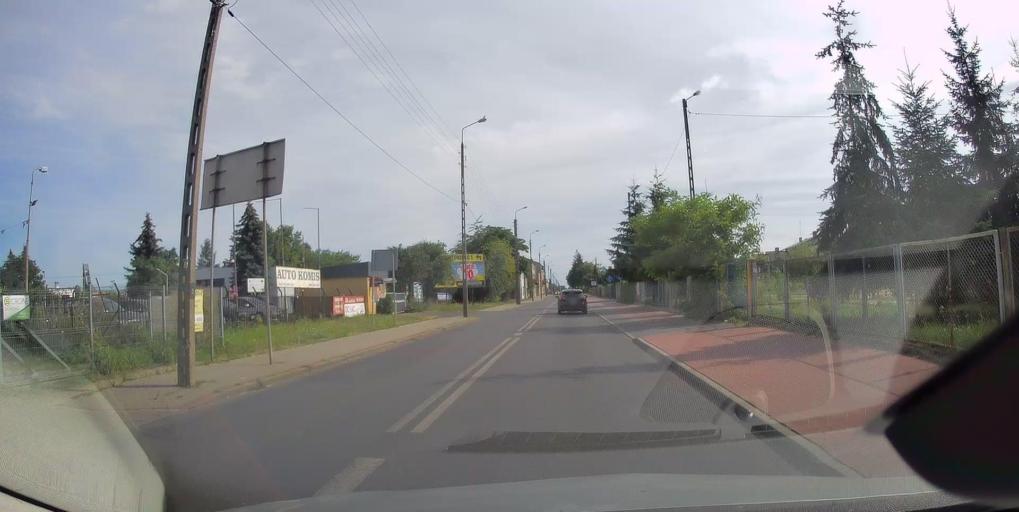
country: PL
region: Lodz Voivodeship
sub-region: Powiat tomaszowski
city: Tomaszow Mazowiecki
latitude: 51.5303
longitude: 19.9970
